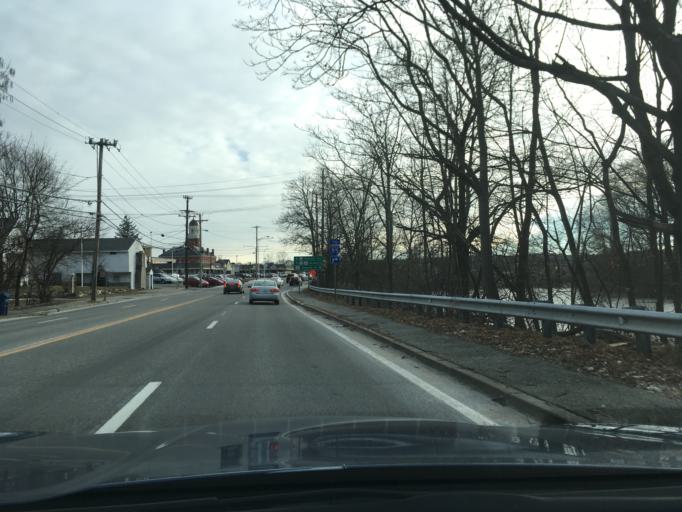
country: US
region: Rhode Island
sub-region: Kent County
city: East Greenwich
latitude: 41.7023
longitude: -71.4608
